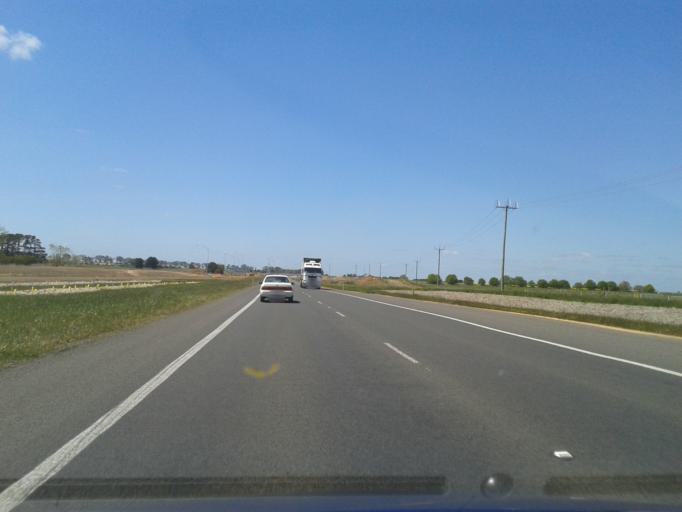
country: AU
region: Victoria
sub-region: Ballarat North
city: Newington
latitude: -37.4532
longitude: 143.5297
